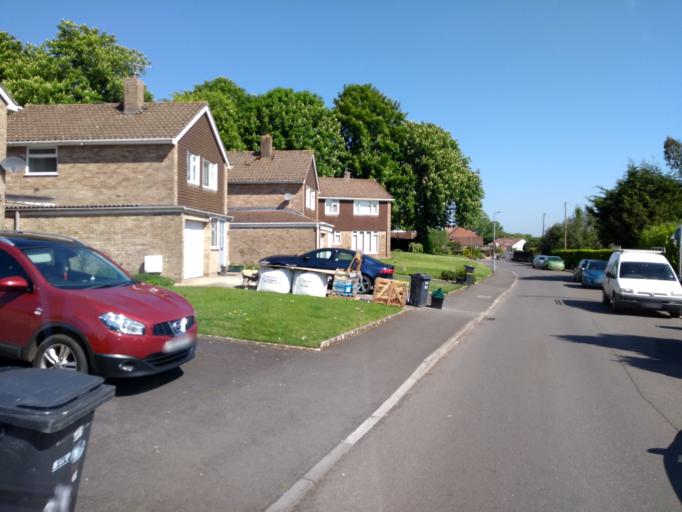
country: GB
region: England
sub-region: Somerset
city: Chard
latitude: 50.8754
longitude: -2.9735
